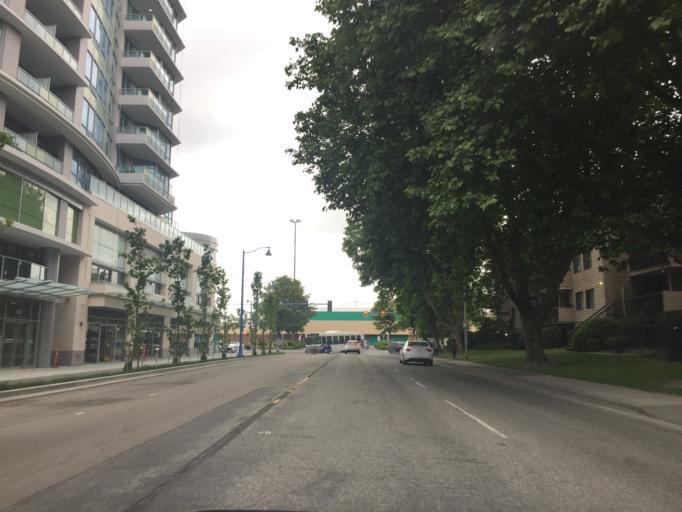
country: CA
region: British Columbia
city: Richmond
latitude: 49.1729
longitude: -123.1316
